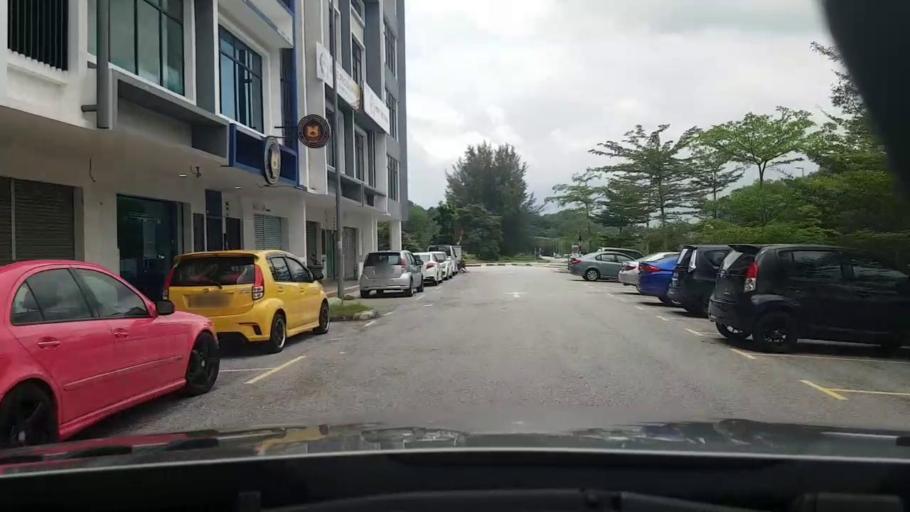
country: MY
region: Selangor
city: Subang Jaya
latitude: 2.9850
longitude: 101.6193
